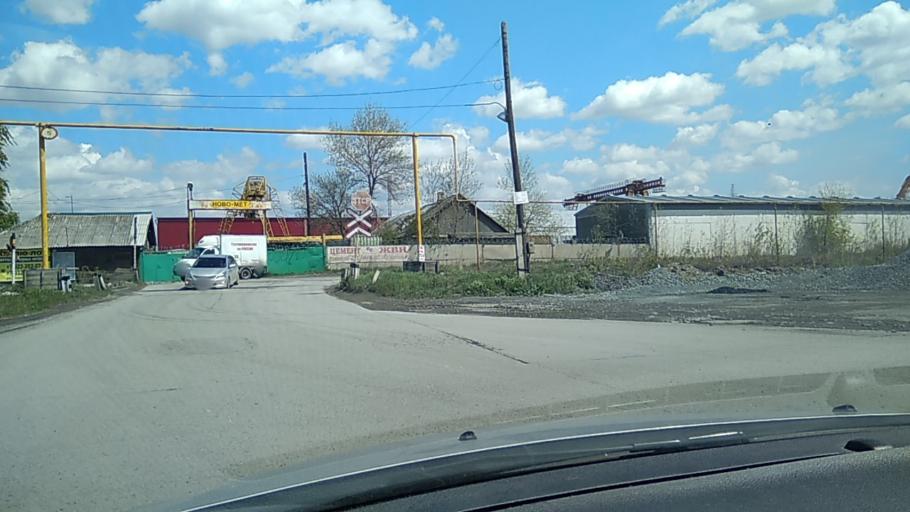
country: RU
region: Sverdlovsk
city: Istok
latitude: 56.7542
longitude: 60.7511
